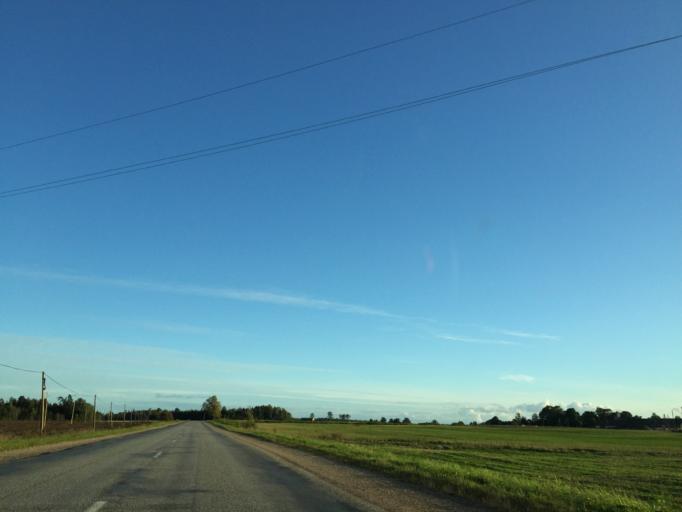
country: LV
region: Saldus Rajons
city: Saldus
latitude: 56.7386
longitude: 22.3773
